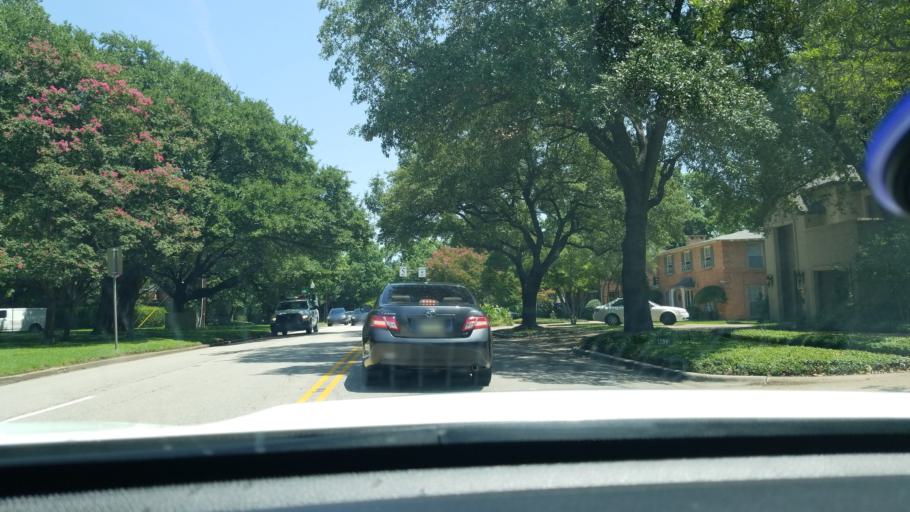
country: US
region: Texas
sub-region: Dallas County
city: University Park
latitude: 32.8367
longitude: -96.8172
